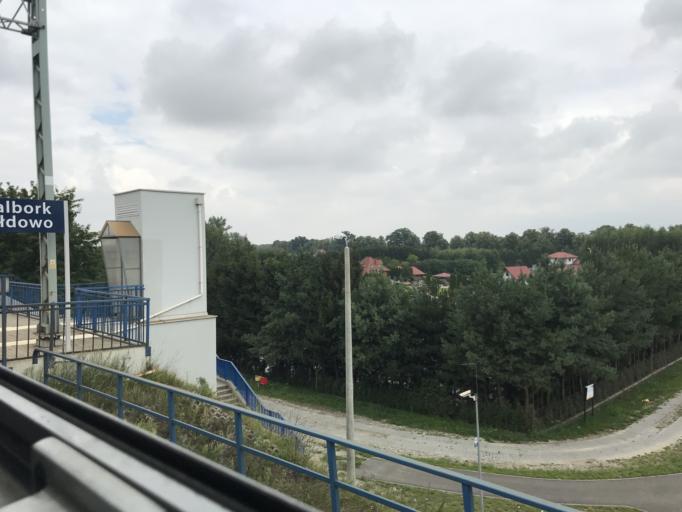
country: PL
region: Pomeranian Voivodeship
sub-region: Powiat malborski
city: Malbork
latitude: 54.0468
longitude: 19.0254
